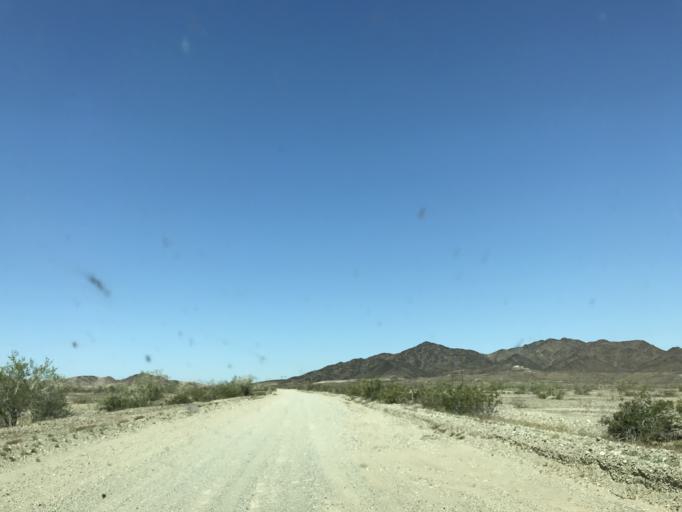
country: US
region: California
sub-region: Riverside County
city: Mesa Verde
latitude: 33.4923
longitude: -114.8115
